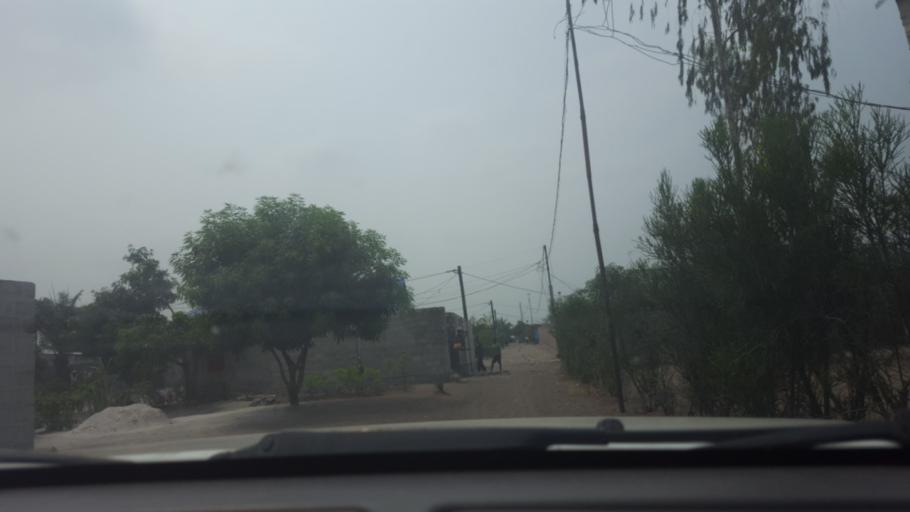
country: CD
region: Kinshasa
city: Masina
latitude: -4.3556
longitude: 15.5088
